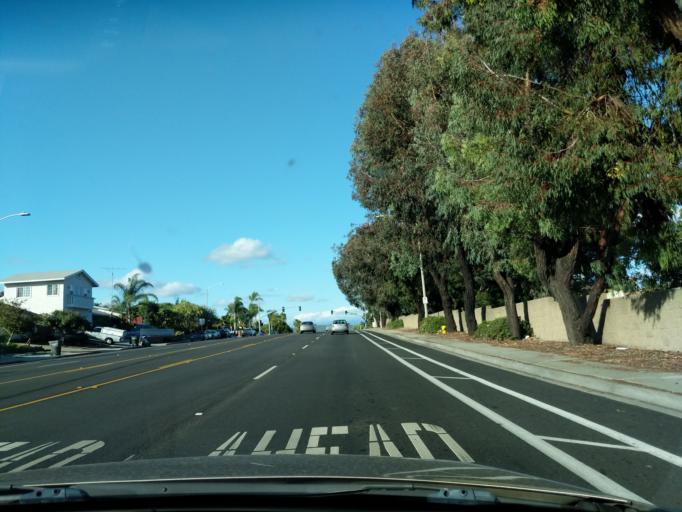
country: US
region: California
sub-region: San Diego County
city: Lake San Marcos
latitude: 33.1256
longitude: -117.2147
